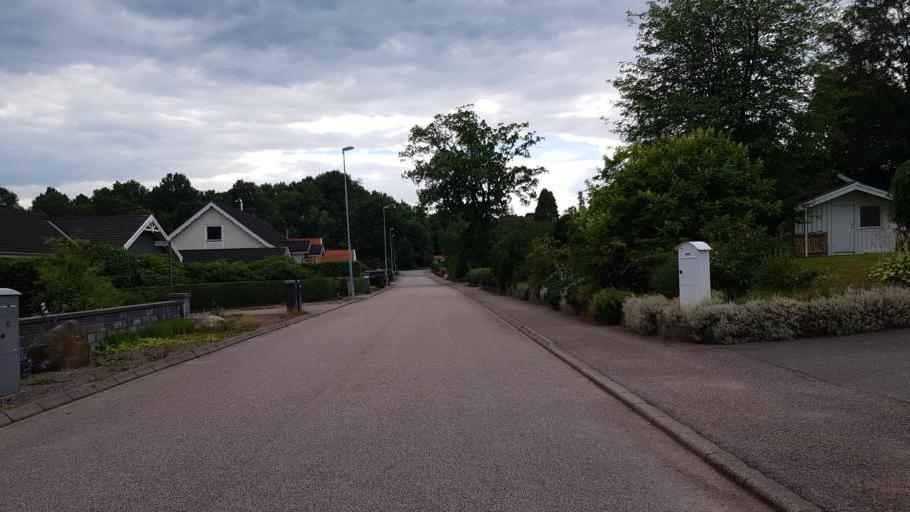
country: SE
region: Vaestra Goetaland
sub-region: Partille Kommun
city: Furulund
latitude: 57.7024
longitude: 12.1387
